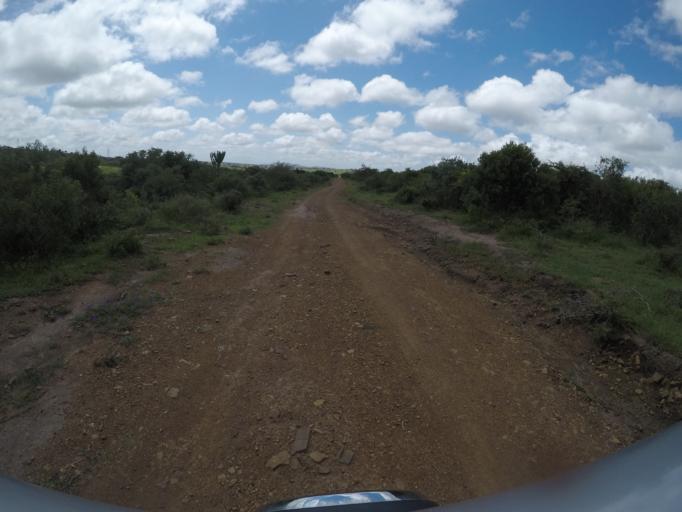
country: ZA
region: KwaZulu-Natal
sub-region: uThungulu District Municipality
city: Empangeni
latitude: -28.5849
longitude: 31.8293
